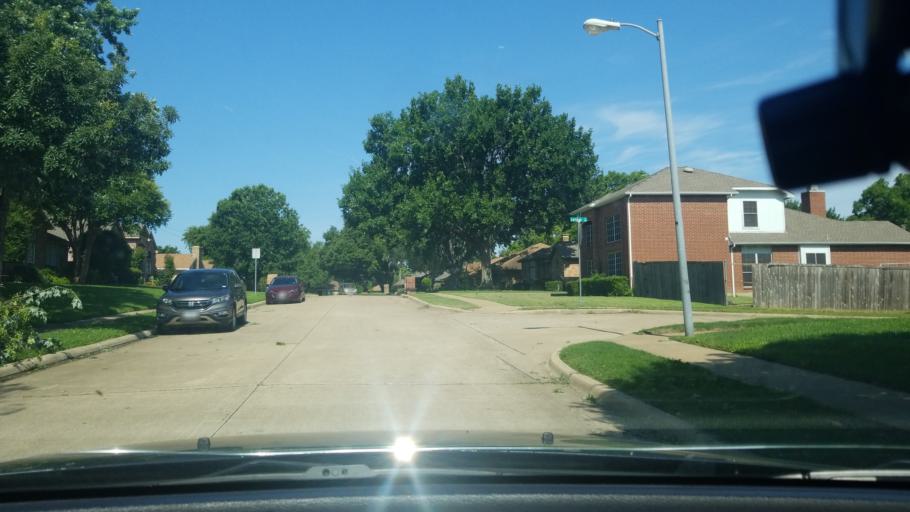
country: US
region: Texas
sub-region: Dallas County
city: Mesquite
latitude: 32.7760
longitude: -96.5905
